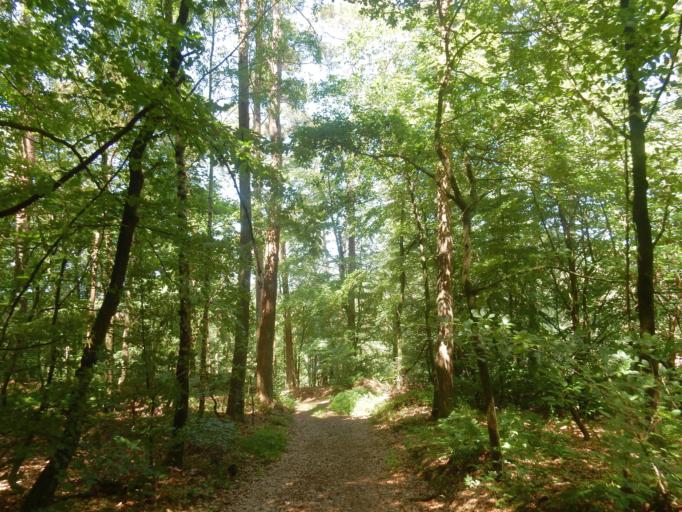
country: LU
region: Luxembourg
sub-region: Canton de Mersch
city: Tuntange
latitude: 49.7431
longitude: 6.0228
